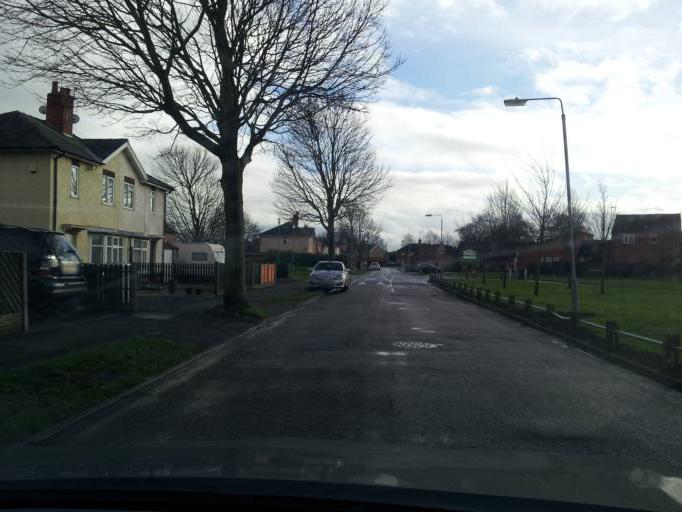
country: GB
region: England
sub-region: Nottinghamshire
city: Newark on Trent
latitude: 53.0656
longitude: -0.8096
